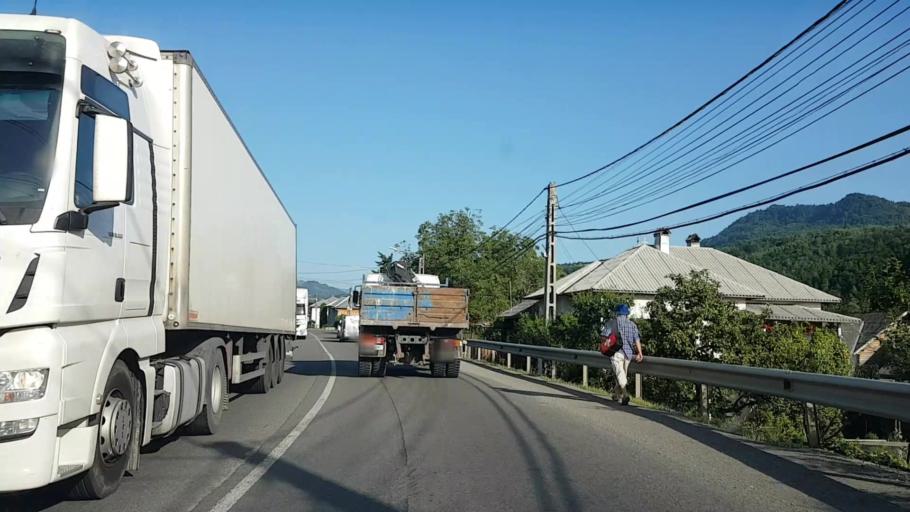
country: RO
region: Bistrita-Nasaud
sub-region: Comuna Tiha Bargaului
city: Tureac
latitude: 47.2279
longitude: 24.8062
